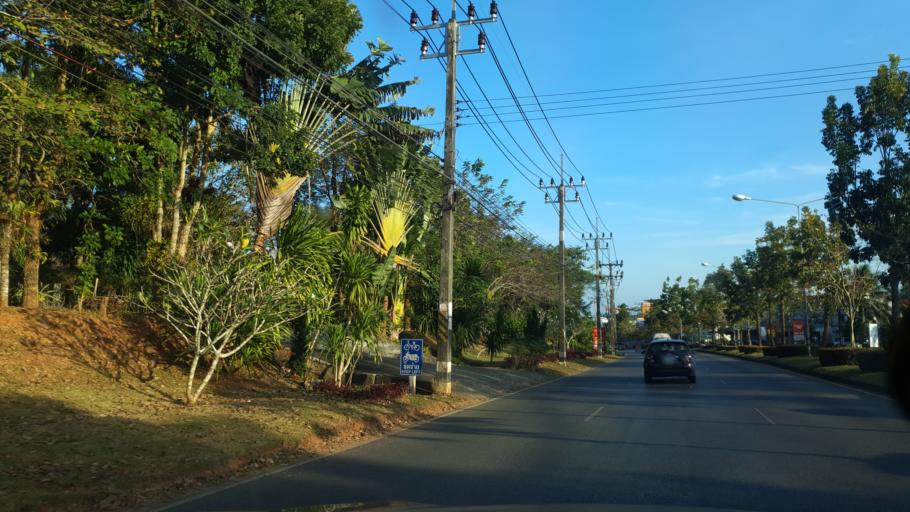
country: TH
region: Krabi
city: Krabi
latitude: 8.0820
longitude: 98.8965
